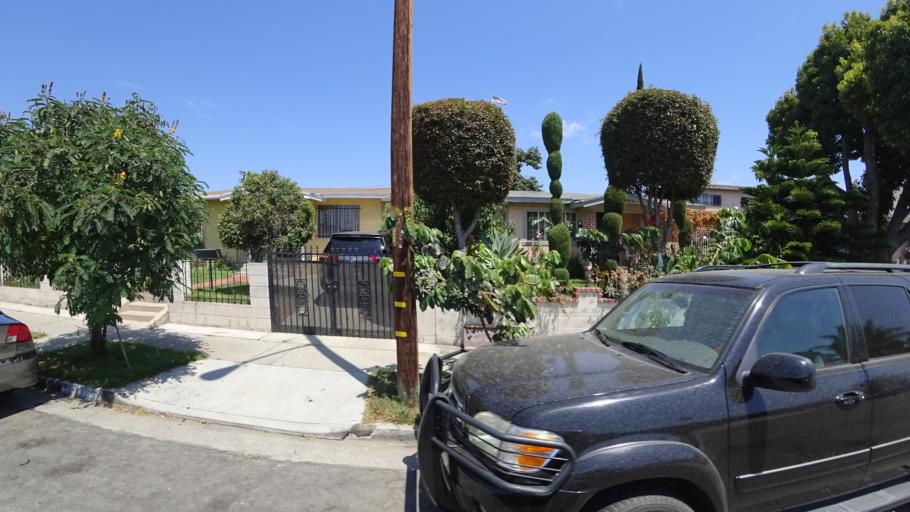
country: US
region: California
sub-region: Los Angeles County
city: Westmont
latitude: 33.9590
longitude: -118.2993
